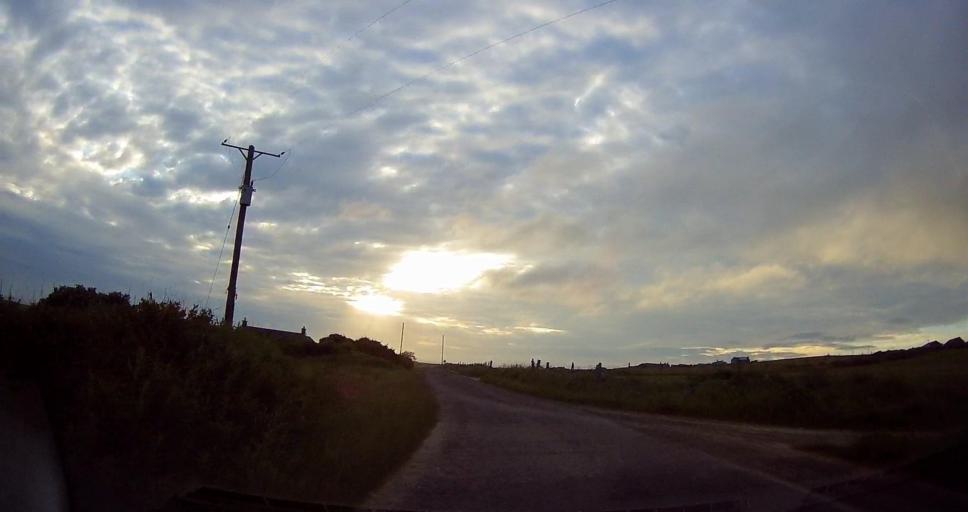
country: GB
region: Scotland
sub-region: Orkney Islands
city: Stromness
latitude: 59.1245
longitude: -3.2794
